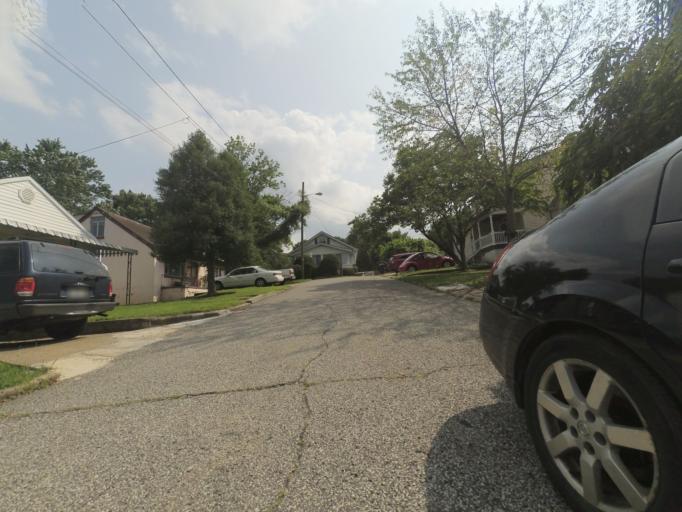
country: US
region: West Virginia
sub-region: Cabell County
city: Huntington
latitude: 38.4047
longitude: -82.4051
